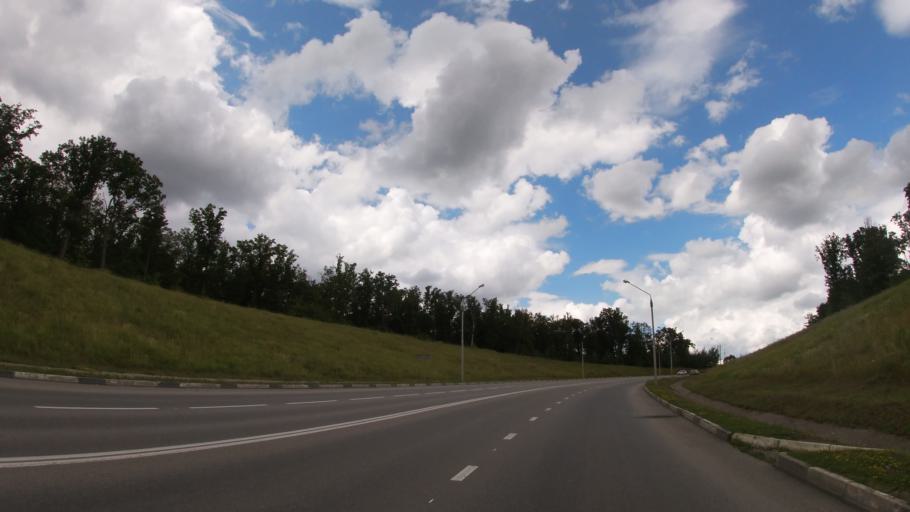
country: RU
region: Belgorod
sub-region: Belgorodskiy Rayon
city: Belgorod
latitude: 50.6231
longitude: 36.6122
